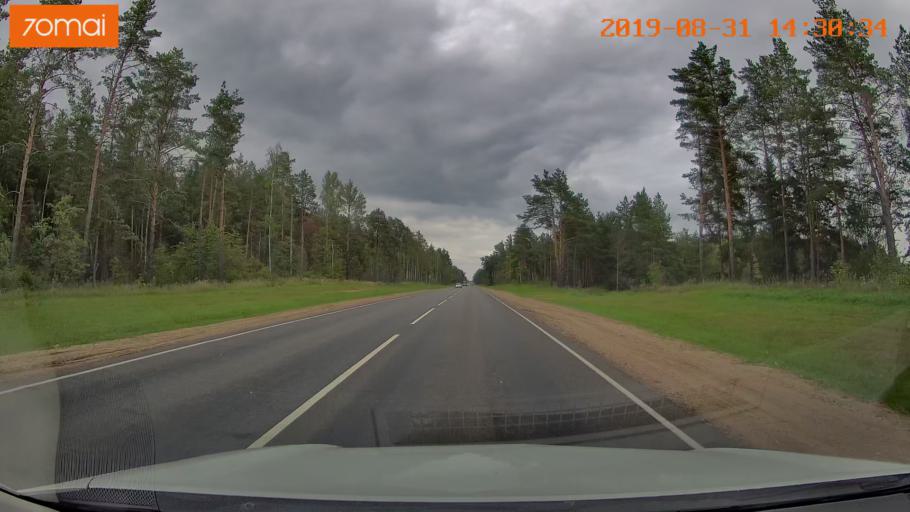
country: RU
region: Smolensk
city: Yekimovichi
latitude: 54.1323
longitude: 33.3533
